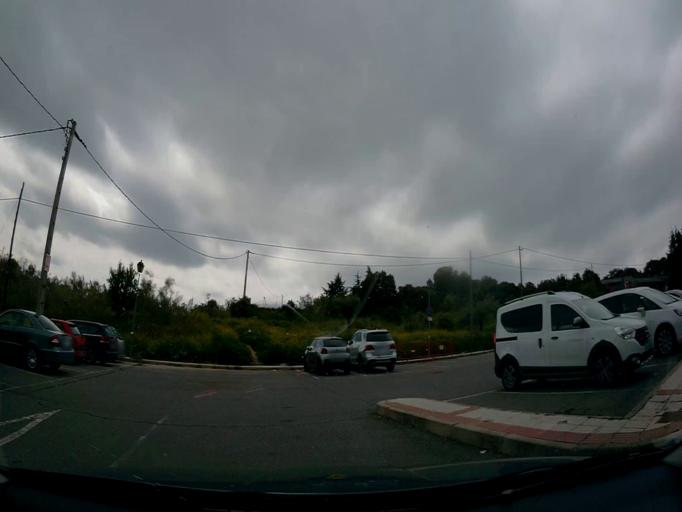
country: ES
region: Madrid
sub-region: Provincia de Madrid
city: Navalagamella
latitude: 40.4675
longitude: -4.1265
